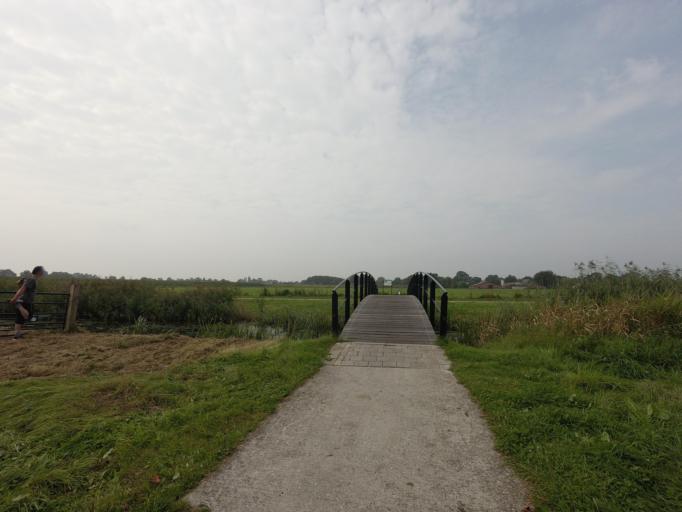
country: NL
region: Gelderland
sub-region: Gemeente Voorst
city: Twello
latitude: 52.2387
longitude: 6.0381
